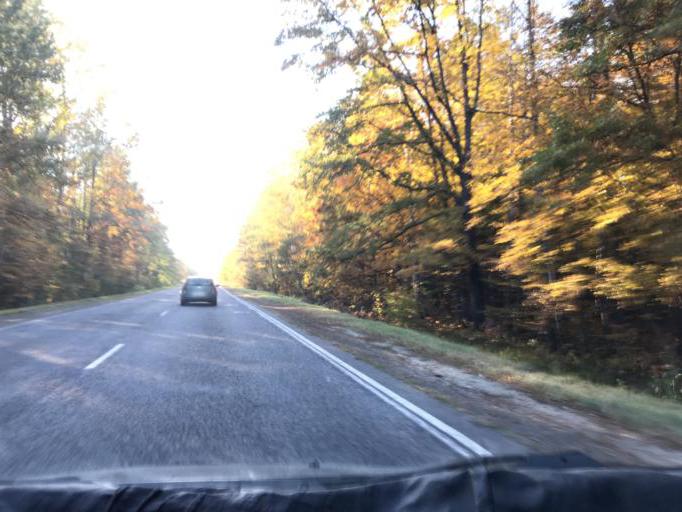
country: BY
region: Gomel
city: Zhytkavichy
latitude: 52.2748
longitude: 28.1784
